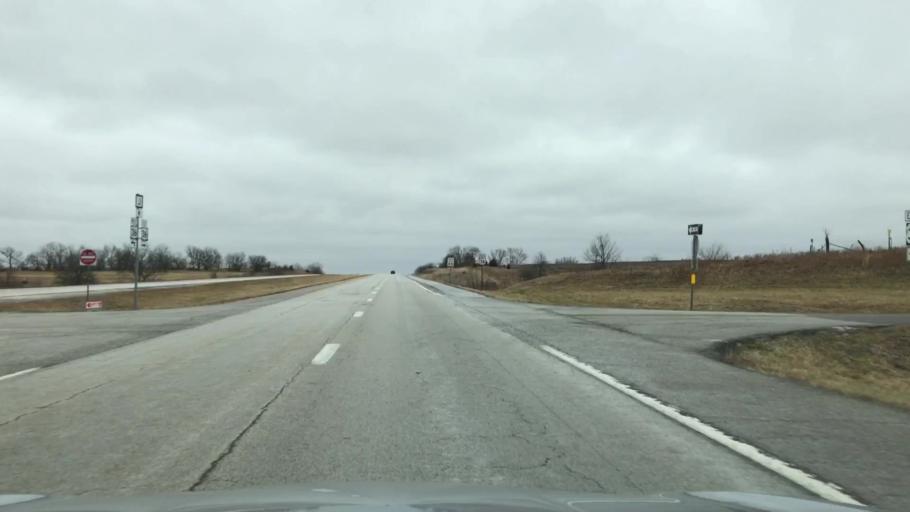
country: US
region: Missouri
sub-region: Caldwell County
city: Hamilton
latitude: 39.7502
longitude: -94.1118
